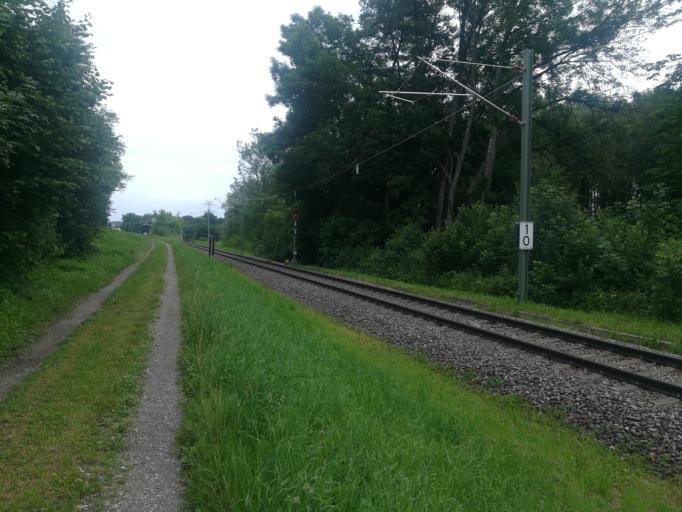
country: DE
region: Baden-Wuerttemberg
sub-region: Freiburg Region
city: Riegel
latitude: 48.1457
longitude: 7.7533
